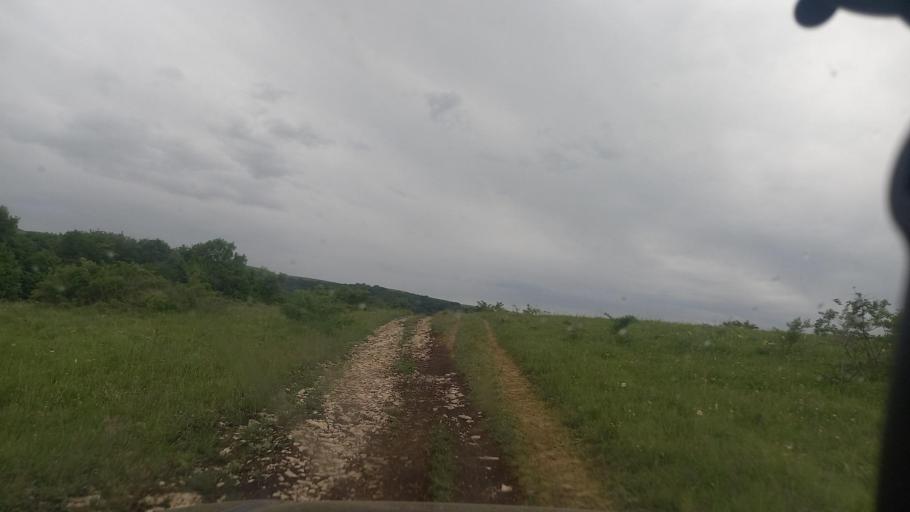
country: RU
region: Karachayevo-Cherkesiya
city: Pregradnaya
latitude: 44.0182
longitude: 41.2829
